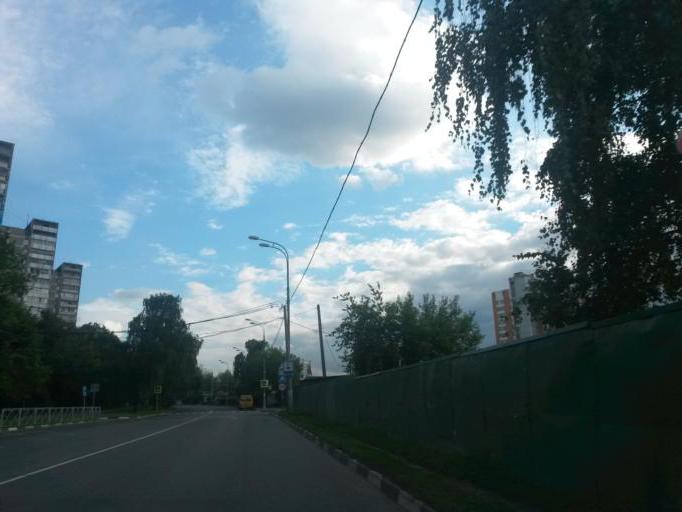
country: RU
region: Moscow
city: Orekhovo-Borisovo
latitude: 55.6250
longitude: 37.7324
